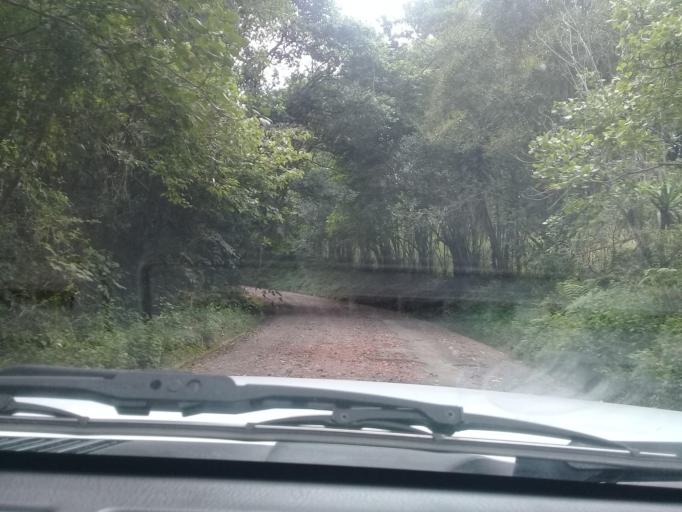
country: MX
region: Veracruz
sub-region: Rafael Lucio
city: Piletas
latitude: 19.5848
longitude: -96.9688
